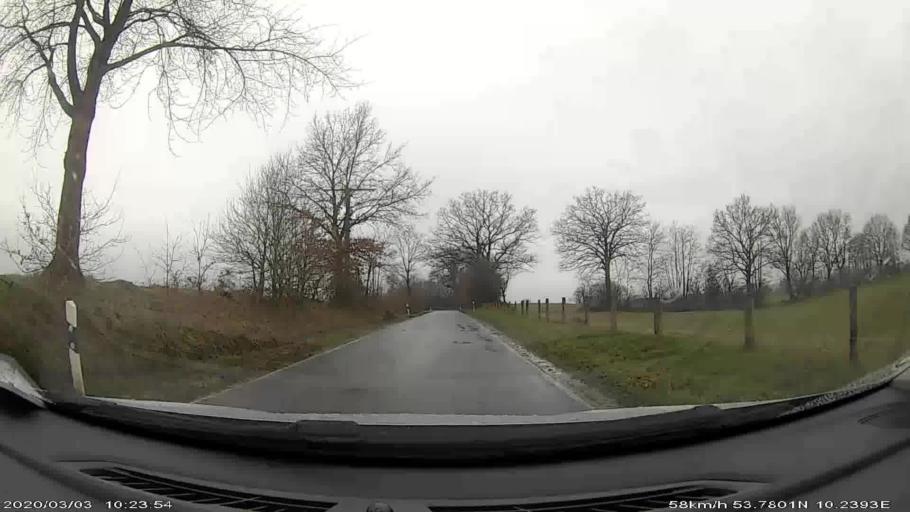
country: DE
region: Schleswig-Holstein
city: Sulfeld
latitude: 53.7788
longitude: 10.2340
